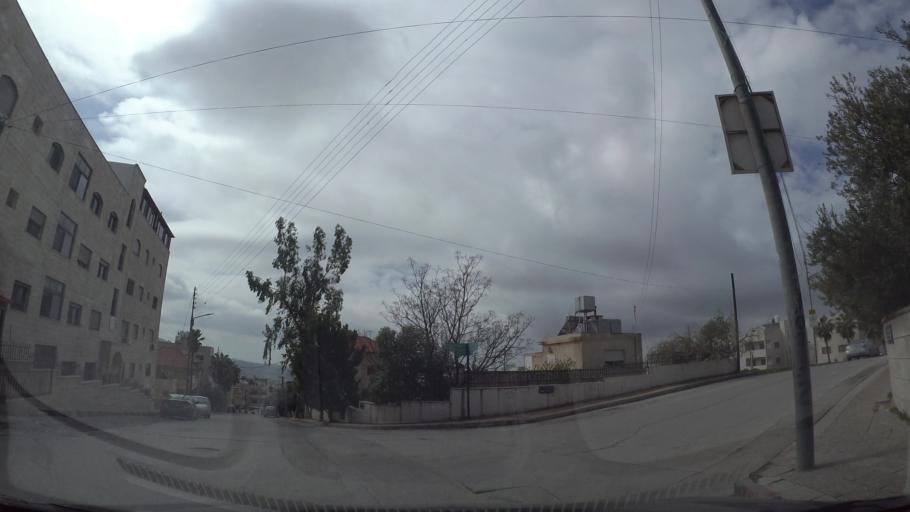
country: JO
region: Amman
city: Wadi as Sir
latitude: 31.9493
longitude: 35.8274
